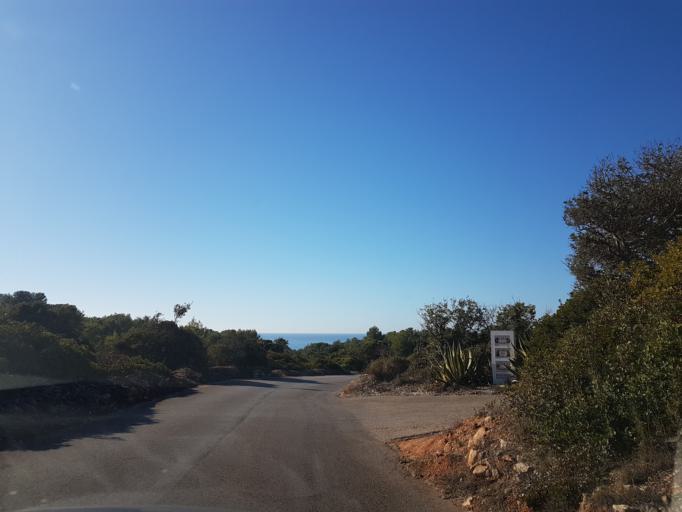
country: PT
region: Faro
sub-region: Lagoa
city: Carvoeiro
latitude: 37.0912
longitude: -8.4207
